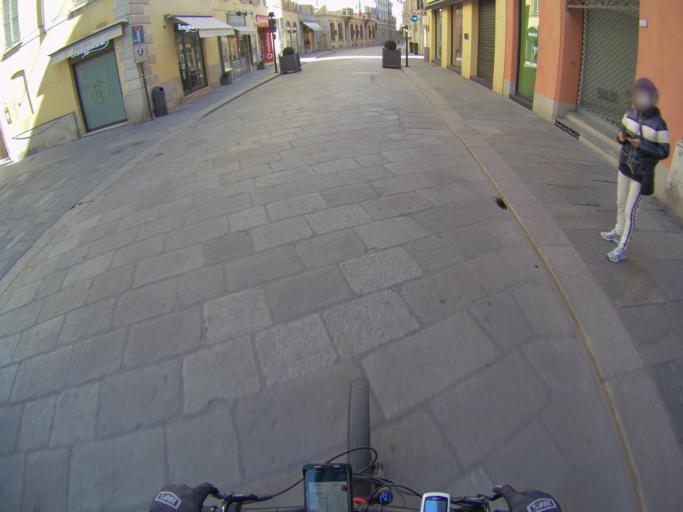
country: IT
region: Emilia-Romagna
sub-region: Provincia di Reggio Emilia
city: Reggio nell'Emilia
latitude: 44.6985
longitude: 10.6317
